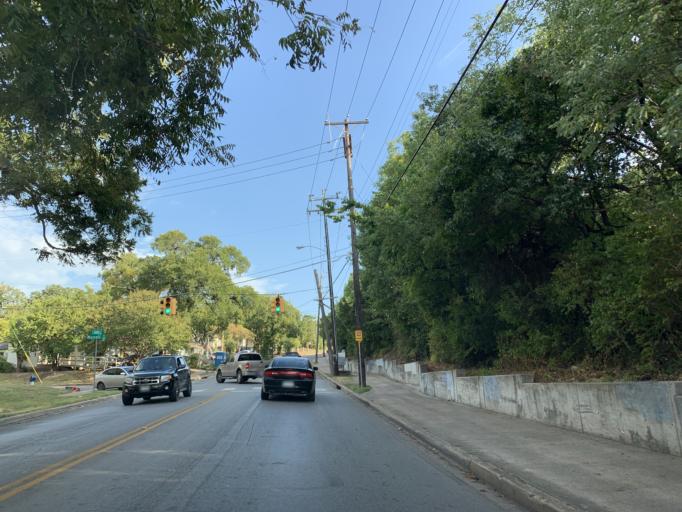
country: US
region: Texas
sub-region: Dallas County
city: Dallas
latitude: 32.7394
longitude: -96.8122
